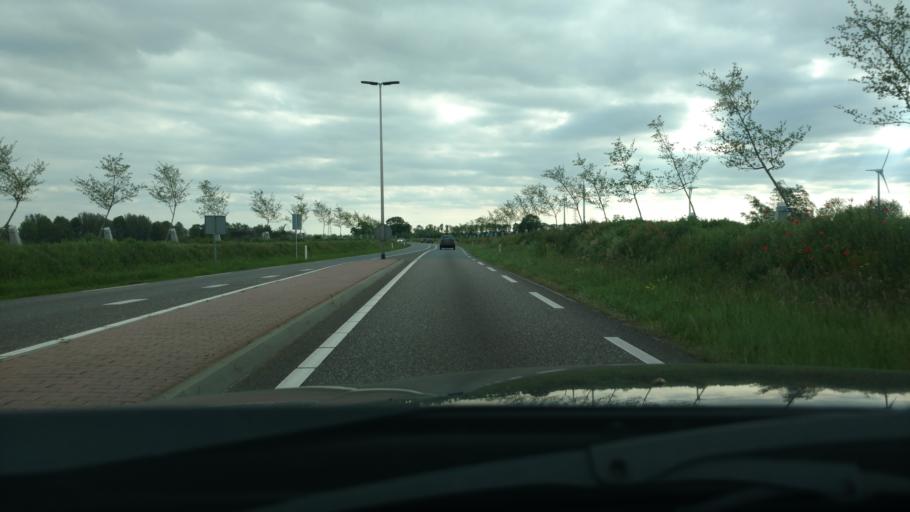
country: NL
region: Gelderland
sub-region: Gemeente Lochem
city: Eefde
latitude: 52.1678
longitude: 6.2090
